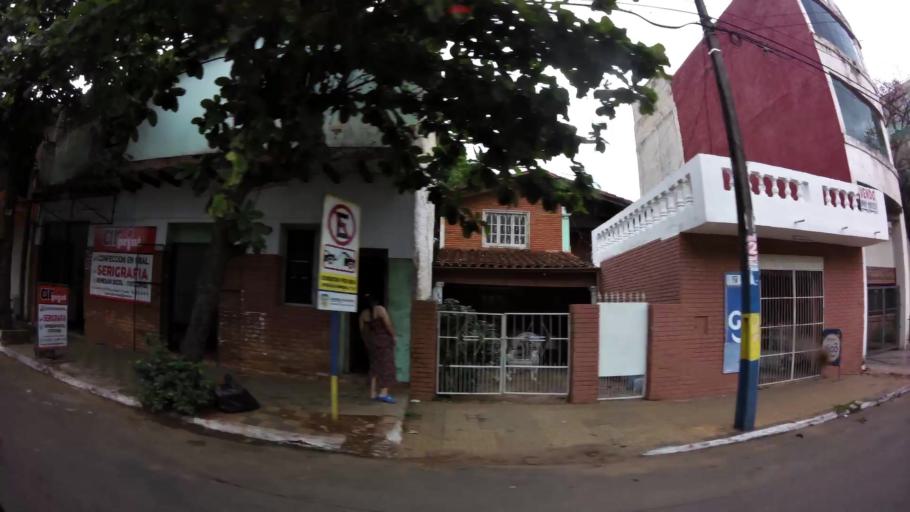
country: PY
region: Central
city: San Lorenzo
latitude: -25.2710
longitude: -57.4935
